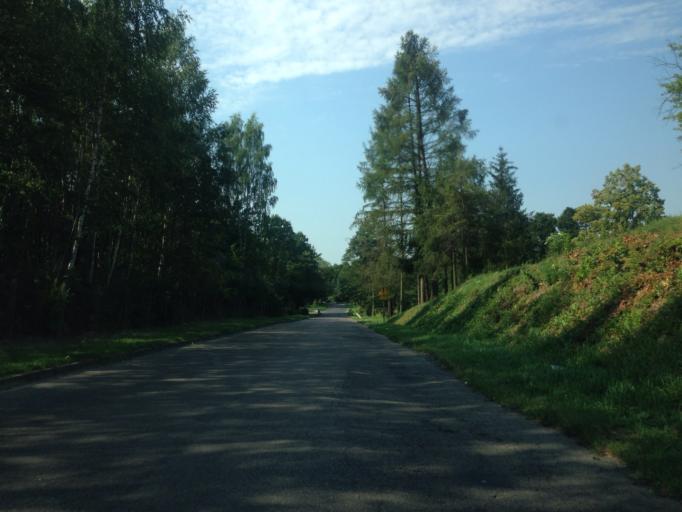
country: PL
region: Kujawsko-Pomorskie
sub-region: Powiat rypinski
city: Rypin
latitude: 53.0803
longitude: 19.4071
